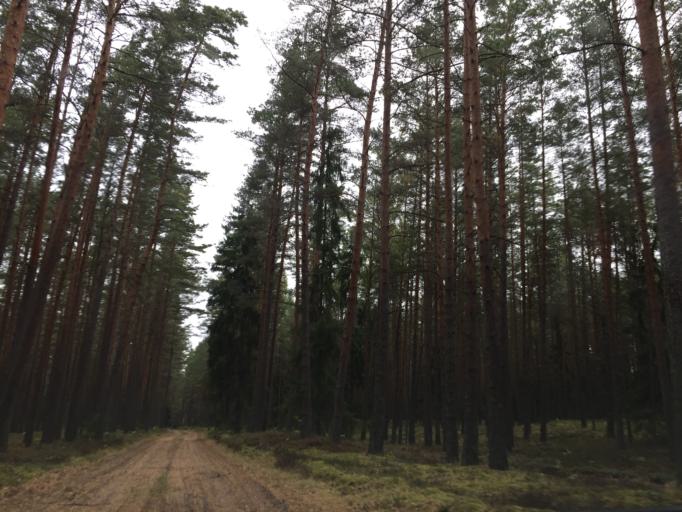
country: LV
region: Salacgrivas
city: Salacgriva
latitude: 57.7076
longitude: 24.3533
